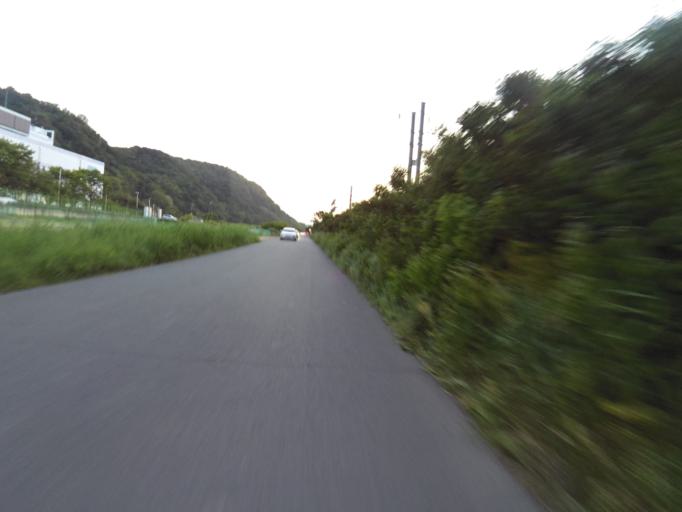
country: KR
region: Gyeongsangbuk-do
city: Gyeongsan-si
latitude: 35.8520
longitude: 128.7020
